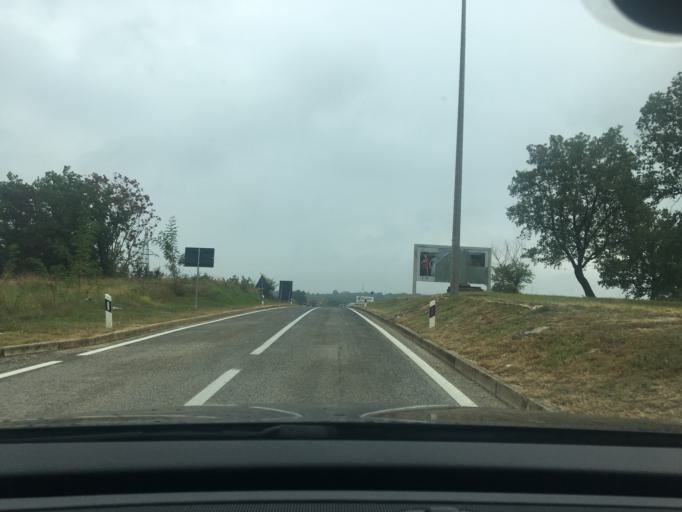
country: HR
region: Istarska
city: Buje
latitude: 45.4171
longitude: 13.6630
